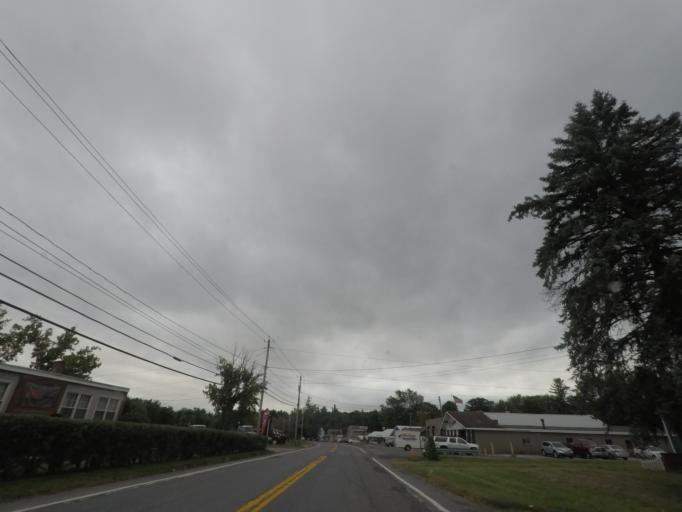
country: US
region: New York
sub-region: Rensselaer County
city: Hoosick Falls
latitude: 42.9165
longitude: -73.3511
